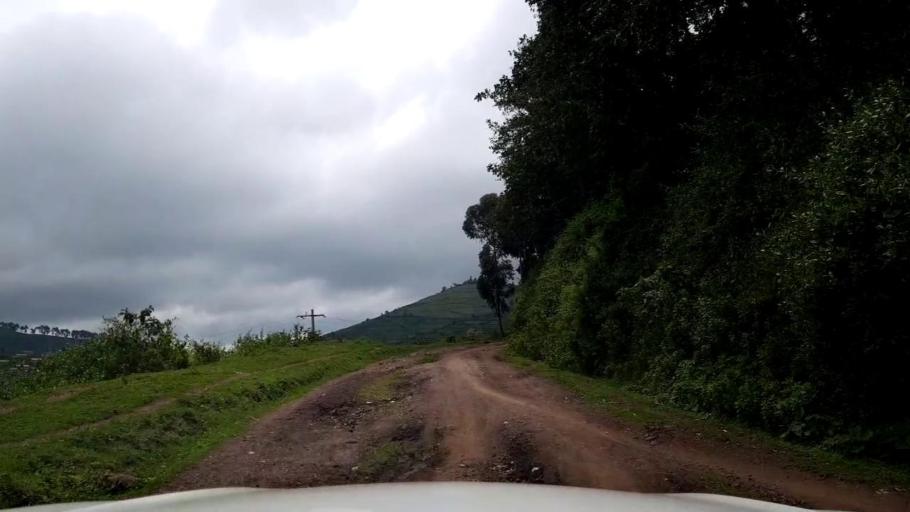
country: RW
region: Western Province
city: Gisenyi
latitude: -1.6632
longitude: 29.4184
